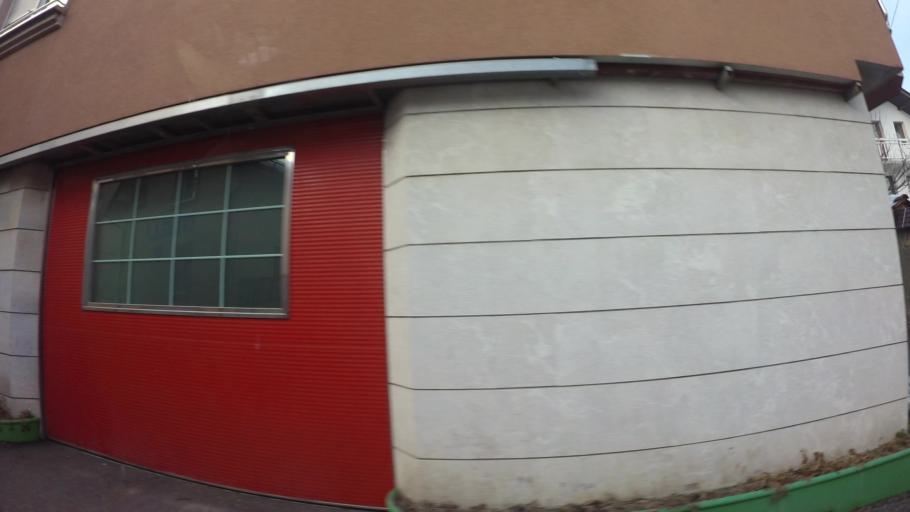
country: BA
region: Federation of Bosnia and Herzegovina
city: Kobilja Glava
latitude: 43.8689
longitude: 18.4284
